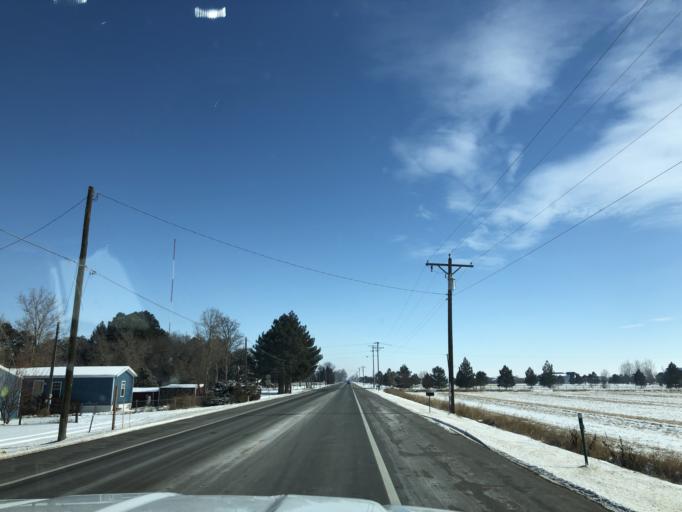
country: US
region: Colorado
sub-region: Morgan County
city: Fort Morgan
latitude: 40.2540
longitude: -103.8507
